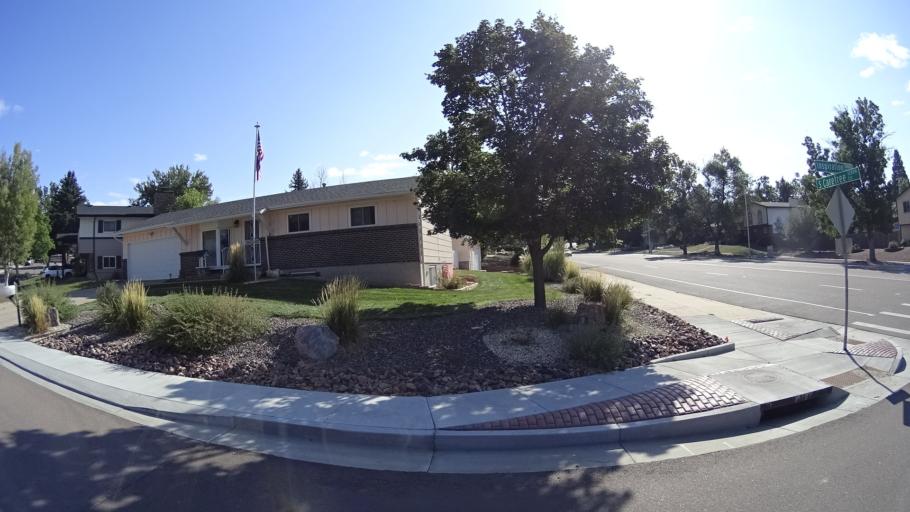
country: US
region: Colorado
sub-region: El Paso County
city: Cimarron Hills
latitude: 38.8780
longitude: -104.7340
